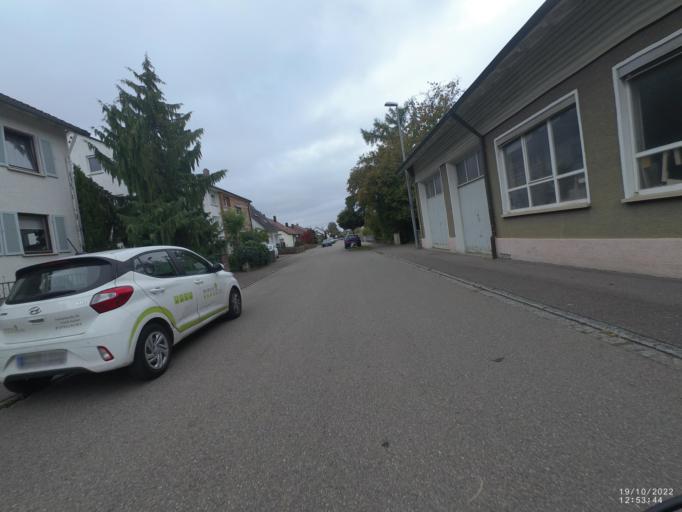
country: DE
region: Baden-Wuerttemberg
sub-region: Regierungsbezirk Stuttgart
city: Sussen
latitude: 48.6740
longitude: 9.7531
